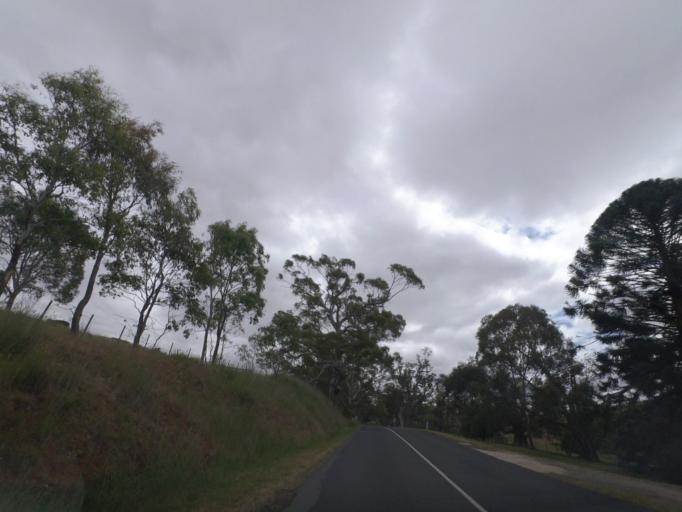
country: AU
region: Victoria
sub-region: Whittlesea
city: Whittlesea
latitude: -37.1975
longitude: 145.0381
